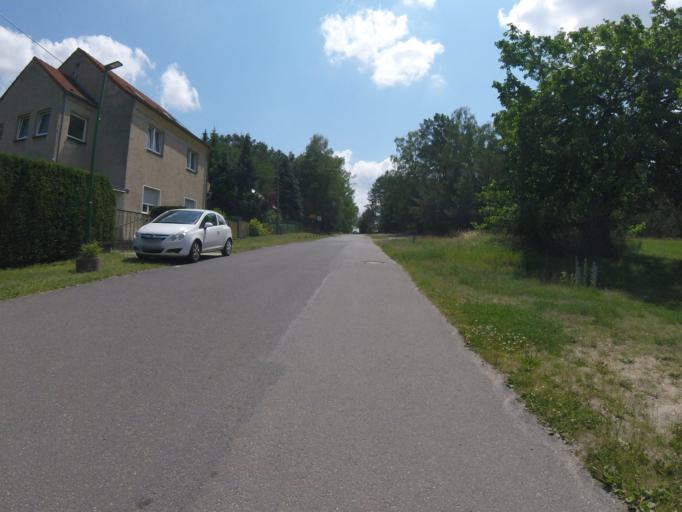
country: DE
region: Brandenburg
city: Bestensee
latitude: 52.2849
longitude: 13.6720
